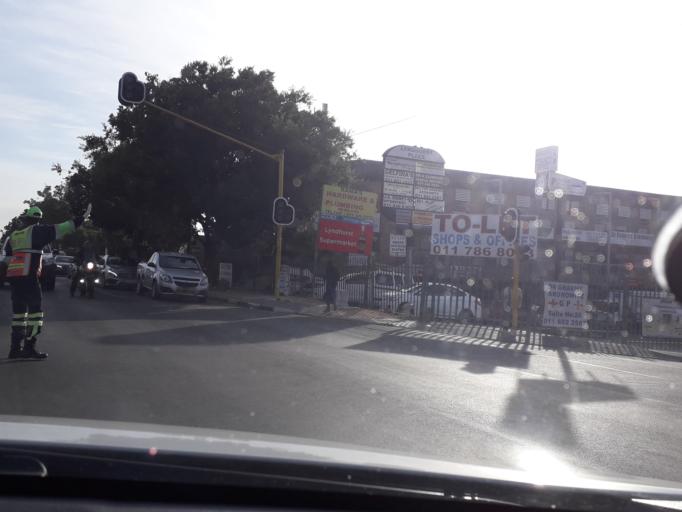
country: ZA
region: Gauteng
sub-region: City of Johannesburg Metropolitan Municipality
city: Modderfontein
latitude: -26.1288
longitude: 28.1031
